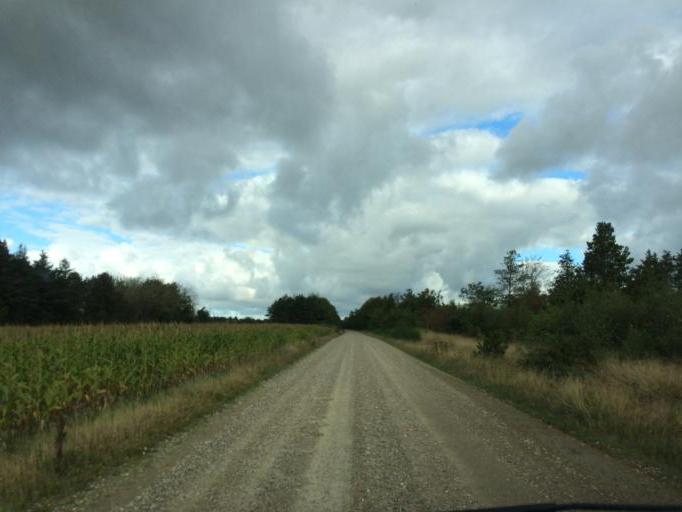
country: DK
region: Central Jutland
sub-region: Holstebro Kommune
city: Ulfborg
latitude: 56.2851
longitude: 8.3894
